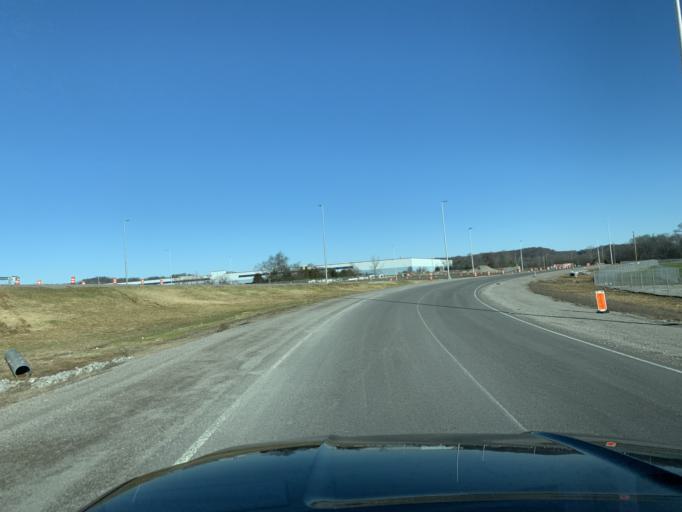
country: US
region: Tennessee
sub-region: Maury County
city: Spring Hill
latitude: 35.7450
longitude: -86.9488
